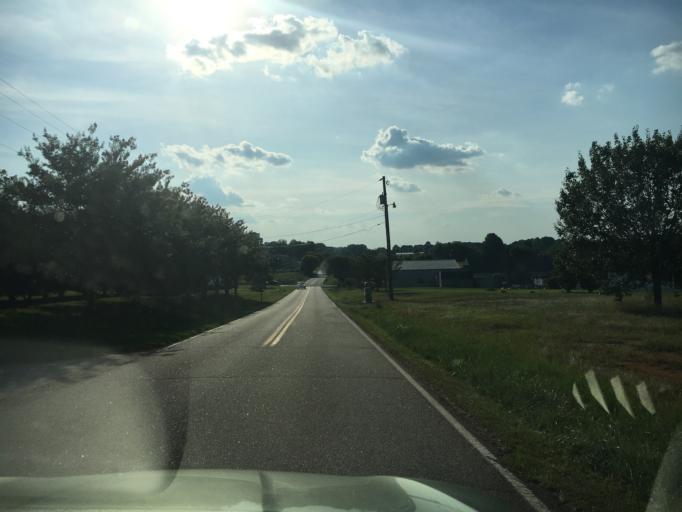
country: US
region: South Carolina
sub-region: Spartanburg County
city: Duncan
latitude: 34.8561
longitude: -82.1170
